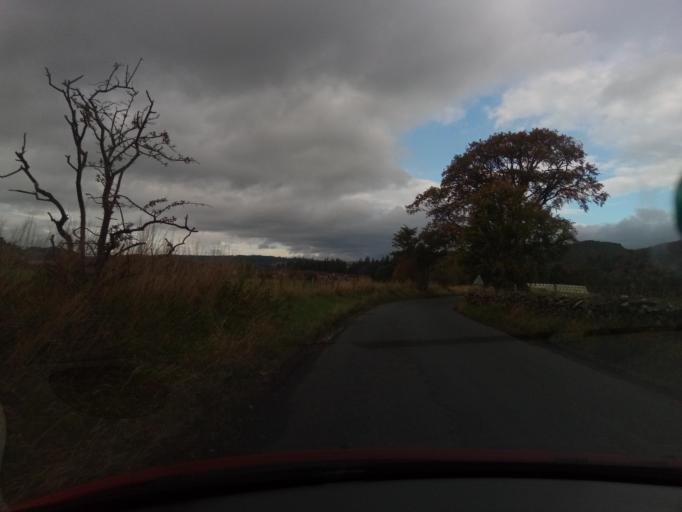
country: GB
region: Scotland
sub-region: The Scottish Borders
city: Peebles
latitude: 55.6423
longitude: -3.1620
